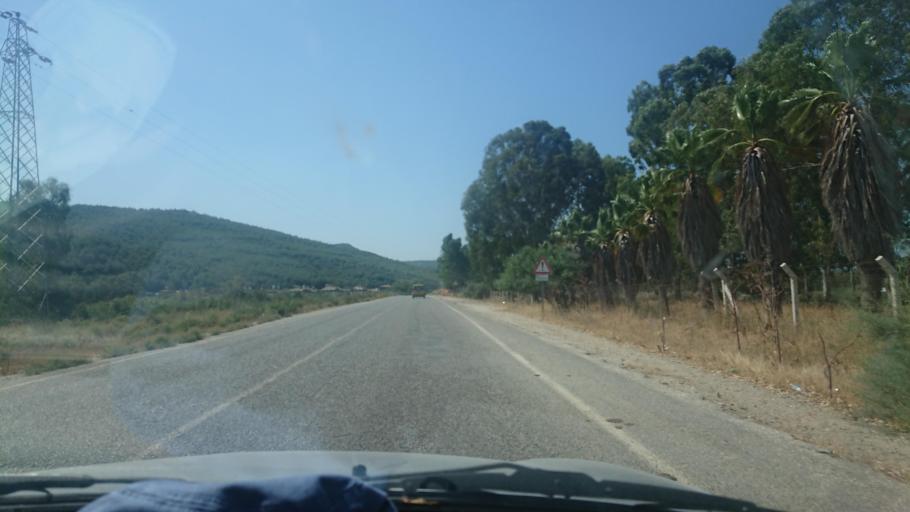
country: TR
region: Izmir
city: Selcuk
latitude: 37.9443
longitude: 27.2795
